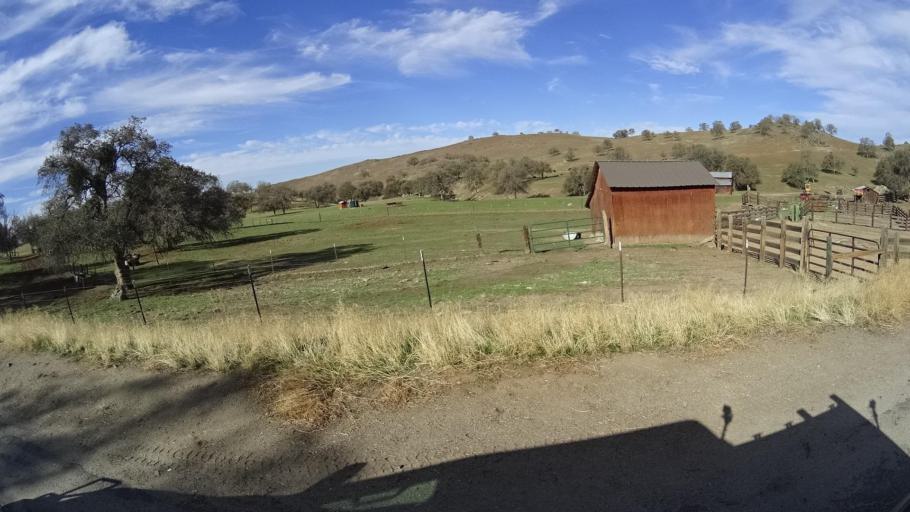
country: US
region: California
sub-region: Kern County
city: Oildale
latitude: 35.5971
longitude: -118.8274
